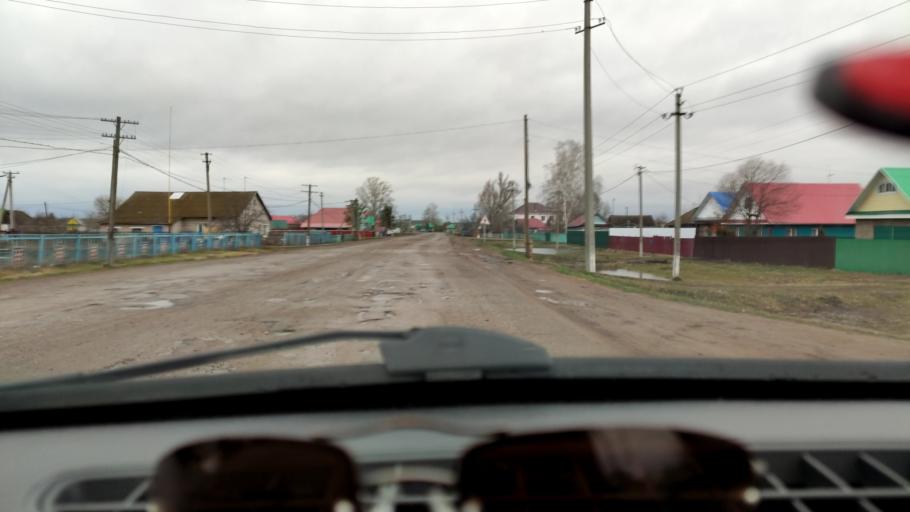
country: RU
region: Bashkortostan
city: Ulukulevo
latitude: 54.4347
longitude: 56.3174
